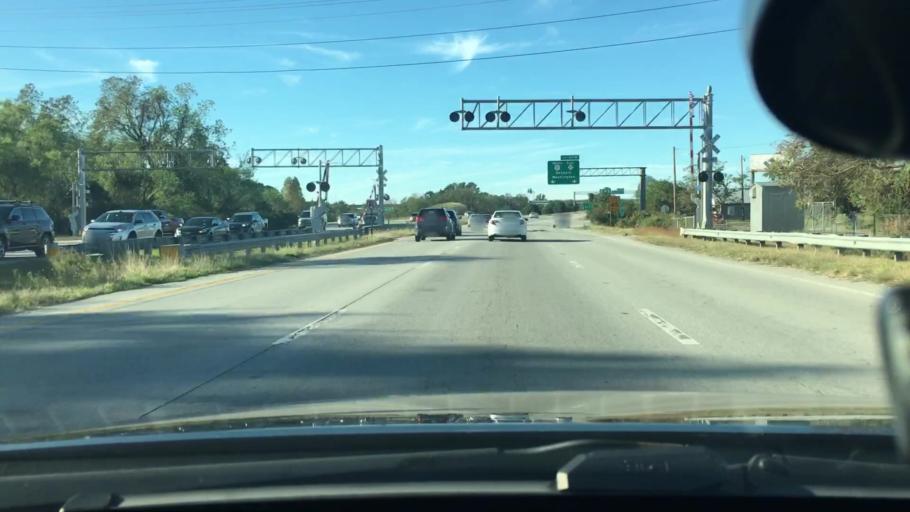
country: US
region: North Carolina
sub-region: Craven County
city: James City
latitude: 35.0883
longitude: -77.0345
